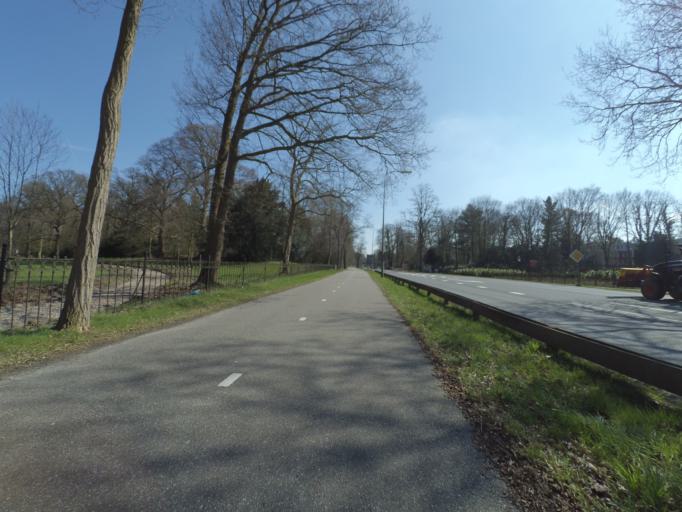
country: NL
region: Utrecht
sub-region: Gemeente Utrechtse Heuvelrug
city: Driebergen-Rijsenburg
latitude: 52.0427
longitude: 5.3040
